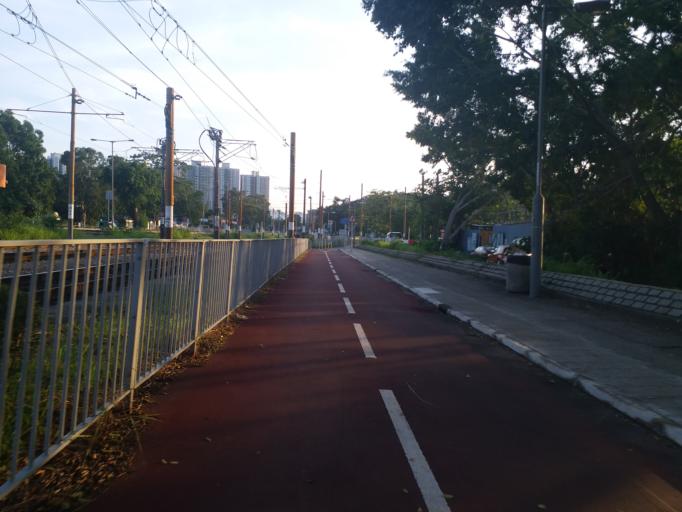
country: HK
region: Yuen Long
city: Yuen Long Kau Hui
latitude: 22.4389
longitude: 114.0050
